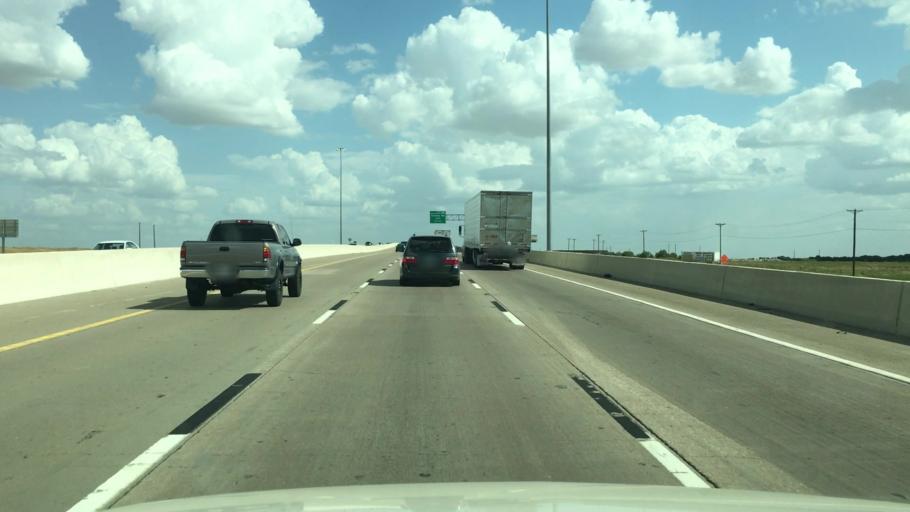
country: US
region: Texas
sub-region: Hill County
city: Hillsboro
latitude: 31.9616
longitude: -97.1175
